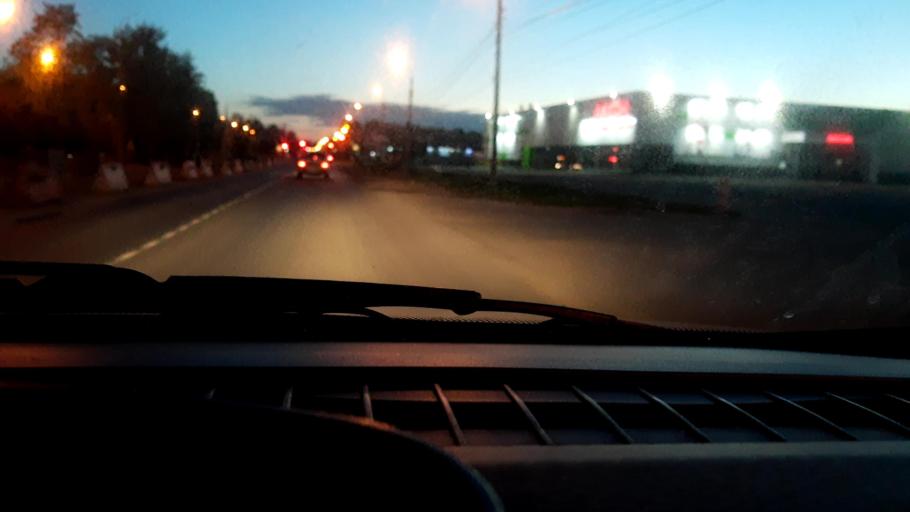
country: RU
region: Nizjnij Novgorod
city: Dzerzhinsk
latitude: 56.2468
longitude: 43.4072
